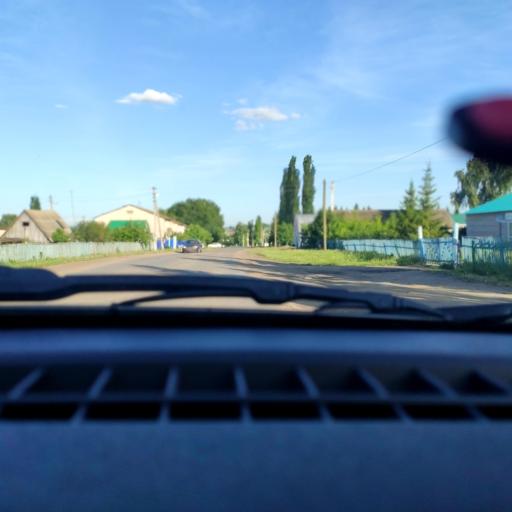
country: RU
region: Bashkortostan
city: Tolbazy
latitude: 54.2927
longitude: 55.8123
